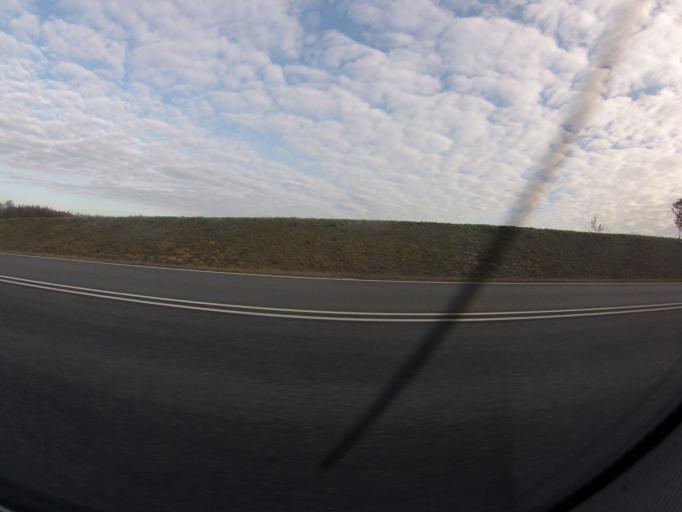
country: DE
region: Thuringia
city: Gossnitz
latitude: 50.8987
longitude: 12.4437
